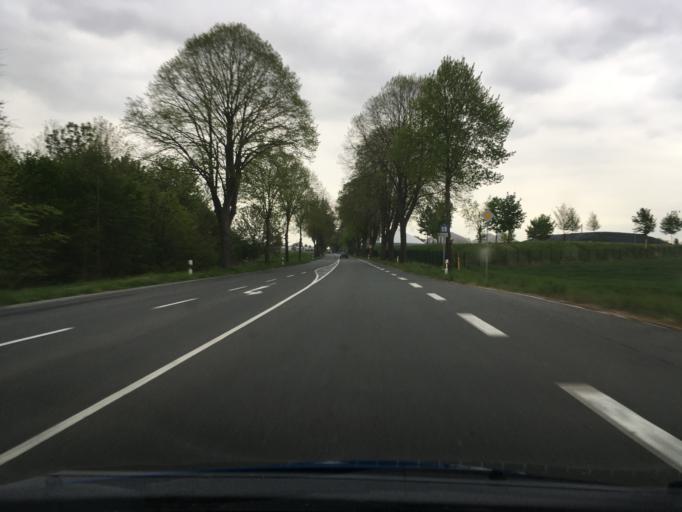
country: DE
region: Lower Saxony
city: Einbeck
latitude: 51.8283
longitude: 9.8378
